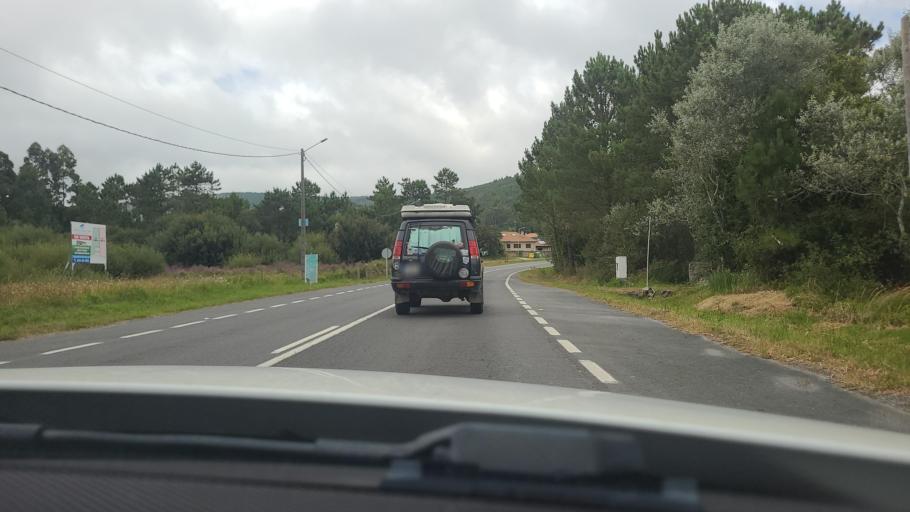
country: ES
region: Galicia
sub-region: Provincia da Coruna
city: Fisterra
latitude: 42.9270
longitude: -9.2589
